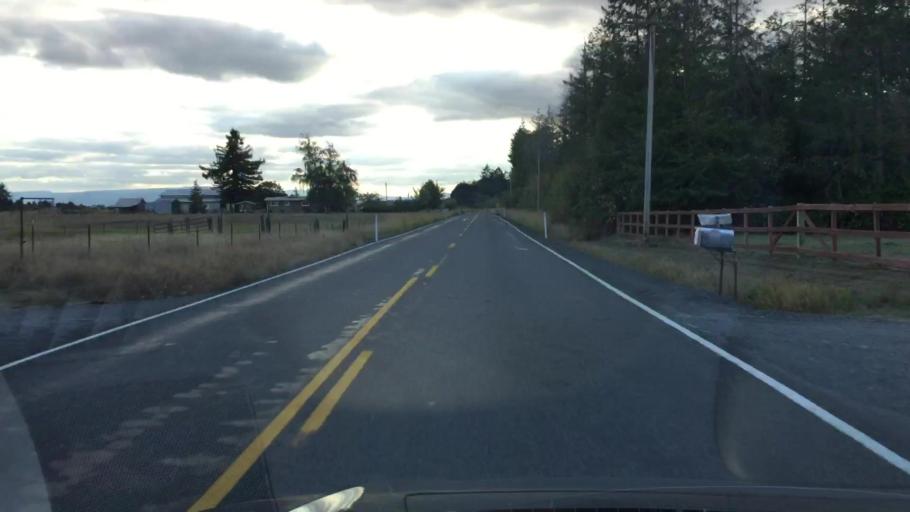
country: US
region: Washington
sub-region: Lewis County
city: Napavine
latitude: 46.4941
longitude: -122.7709
